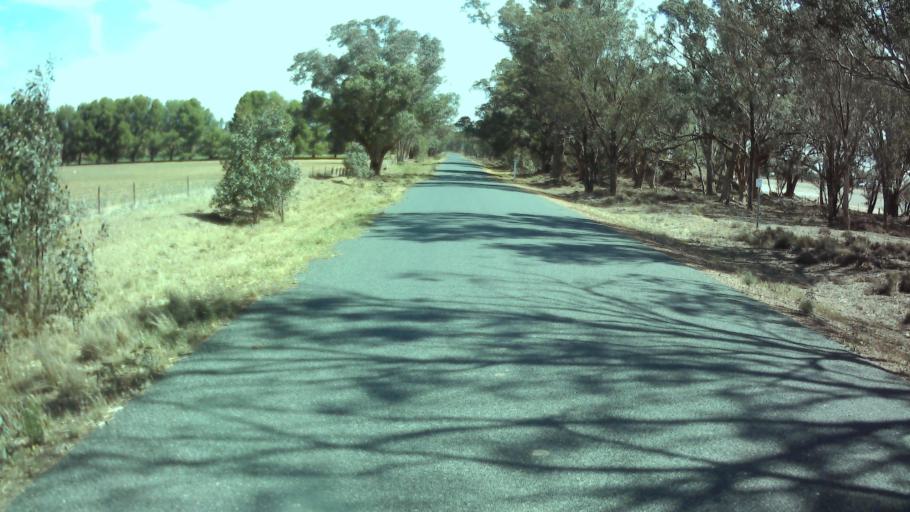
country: AU
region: New South Wales
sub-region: Weddin
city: Grenfell
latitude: -34.0423
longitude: 148.1331
